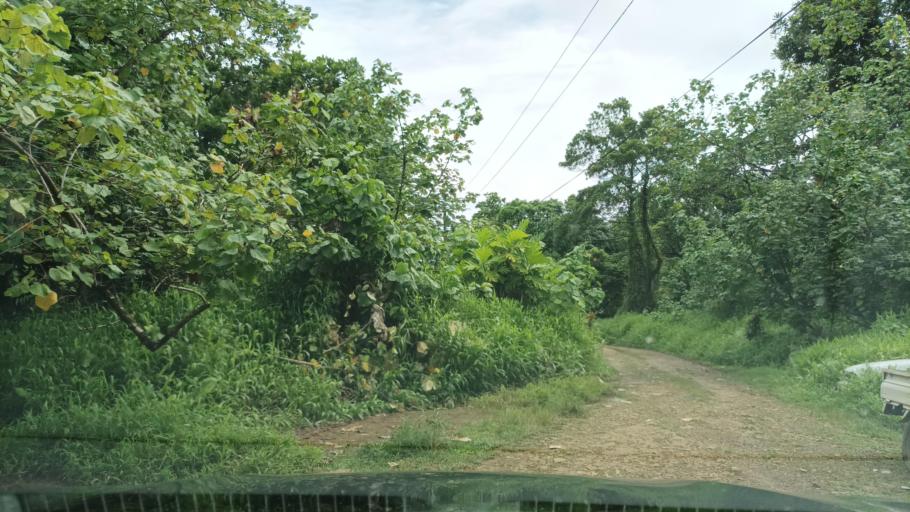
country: FM
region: Pohnpei
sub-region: Madolenihm Municipality
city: Madolenihm Municipality Government
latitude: 6.8256
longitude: 158.2810
